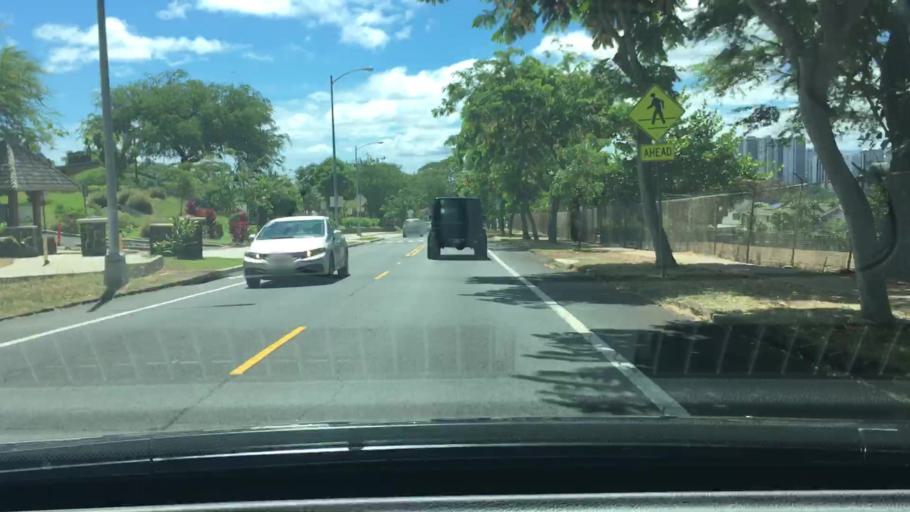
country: US
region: Hawaii
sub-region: Honolulu County
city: Honolulu
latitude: 21.2696
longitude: -157.8052
